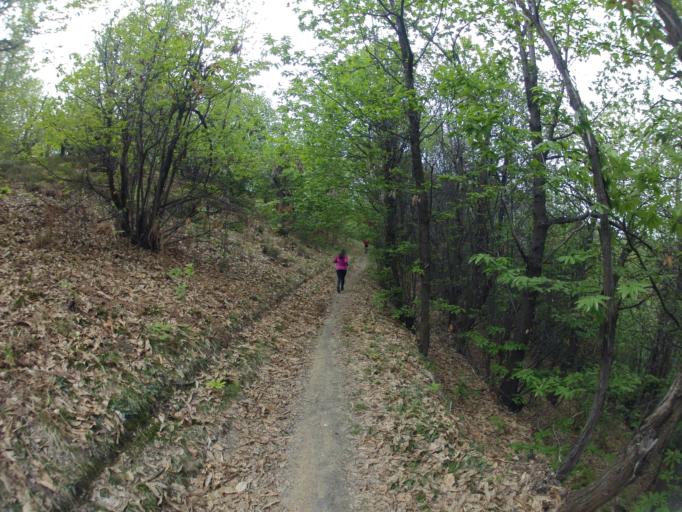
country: IT
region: Piedmont
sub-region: Provincia di Cuneo
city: Peveragno
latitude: 44.3238
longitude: 7.5900
